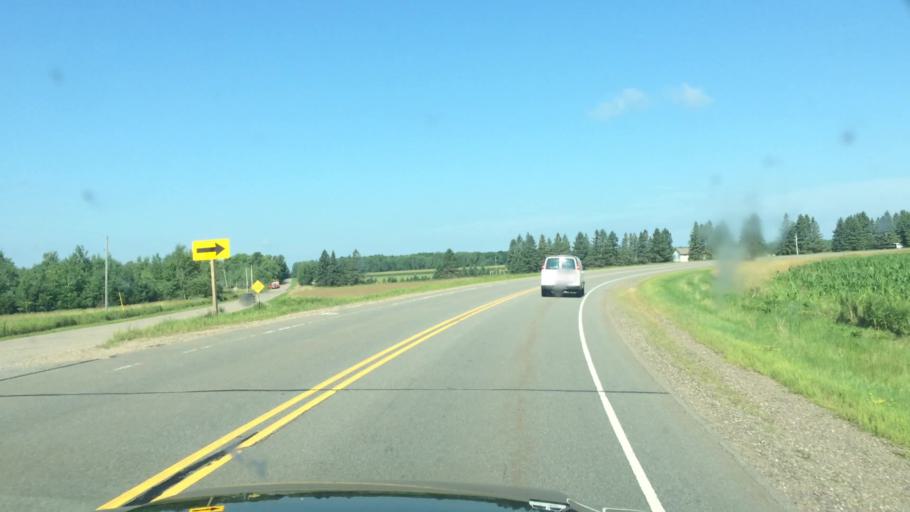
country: US
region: Wisconsin
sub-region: Lincoln County
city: Merrill
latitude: 45.1485
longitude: -89.4631
